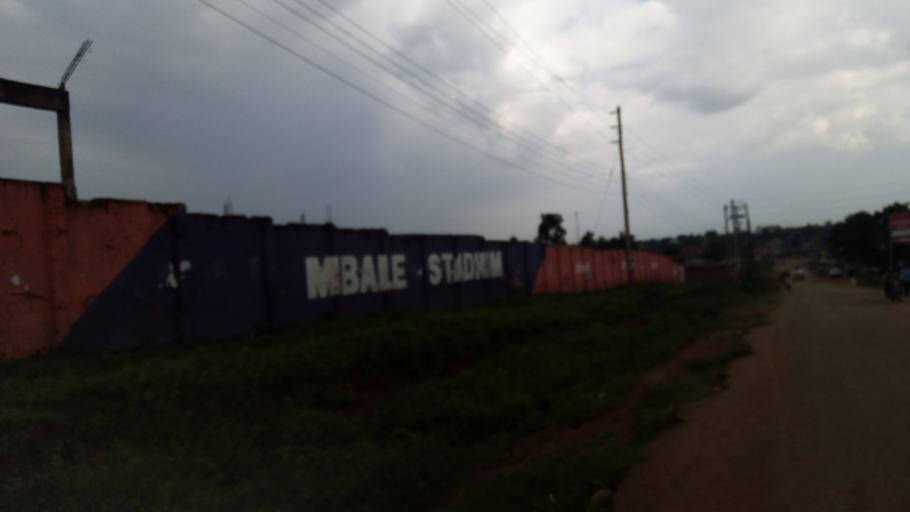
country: UG
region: Eastern Region
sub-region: Mbale District
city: Mbale
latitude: 1.0780
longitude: 34.1650
